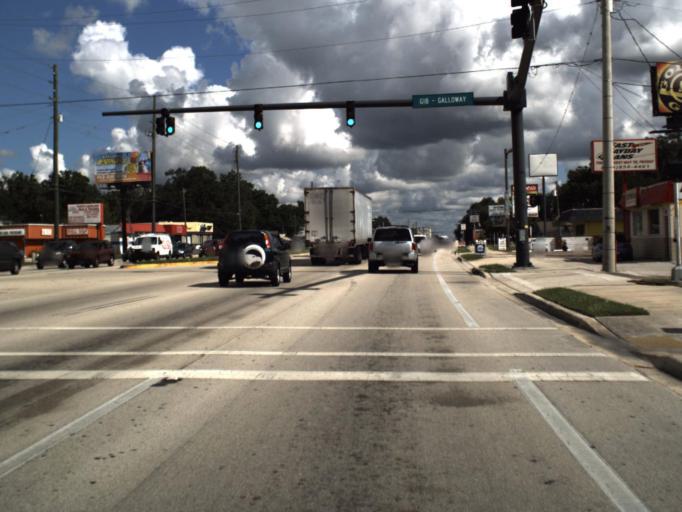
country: US
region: Florida
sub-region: Polk County
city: Gibsonia
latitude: 28.1132
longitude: -81.9736
